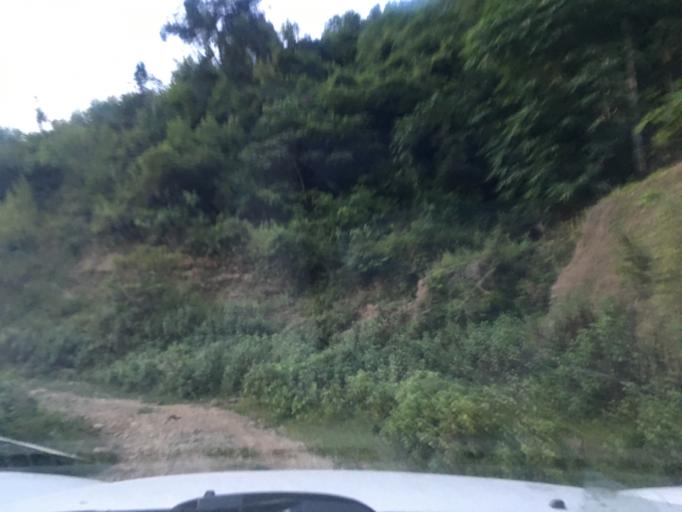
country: CN
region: Guangxi Zhuangzu Zizhiqu
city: Xinzhou
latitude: 25.3546
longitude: 105.7445
